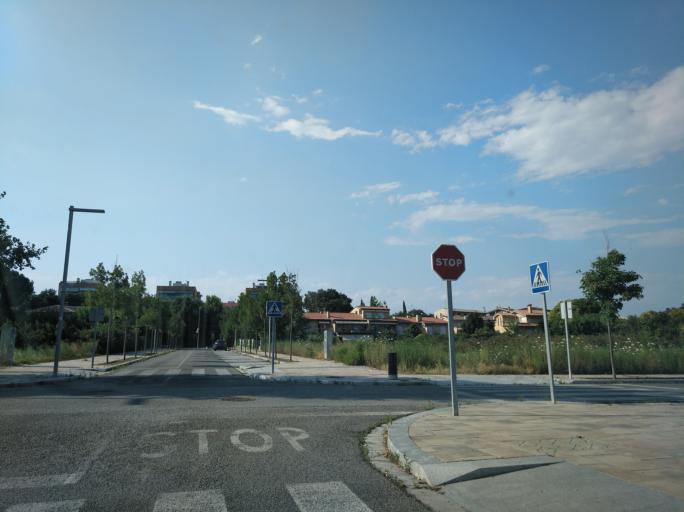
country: ES
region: Catalonia
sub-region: Provincia de Girona
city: Salt
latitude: 41.9908
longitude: 2.8042
